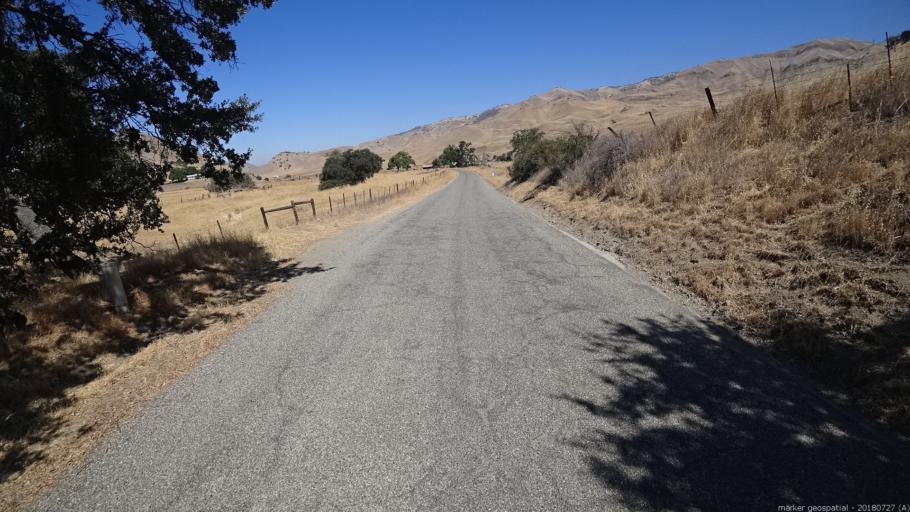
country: US
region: California
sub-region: Monterey County
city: King City
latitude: 36.3000
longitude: -120.9044
